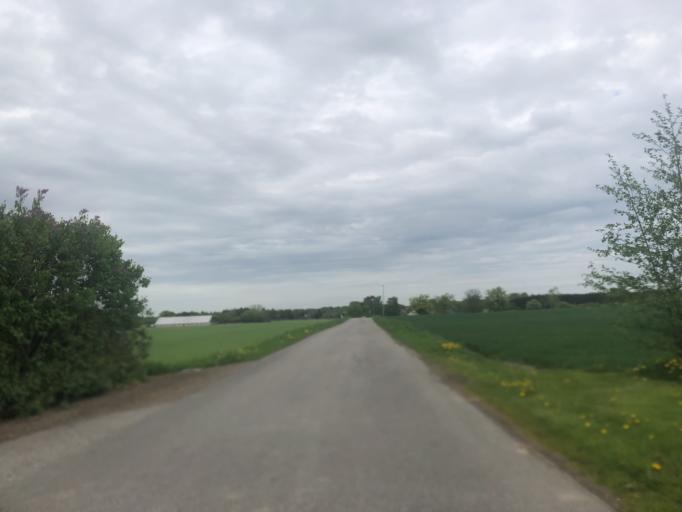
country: DK
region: Zealand
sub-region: Koge Kommune
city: Ejby
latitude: 55.4577
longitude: 12.1024
